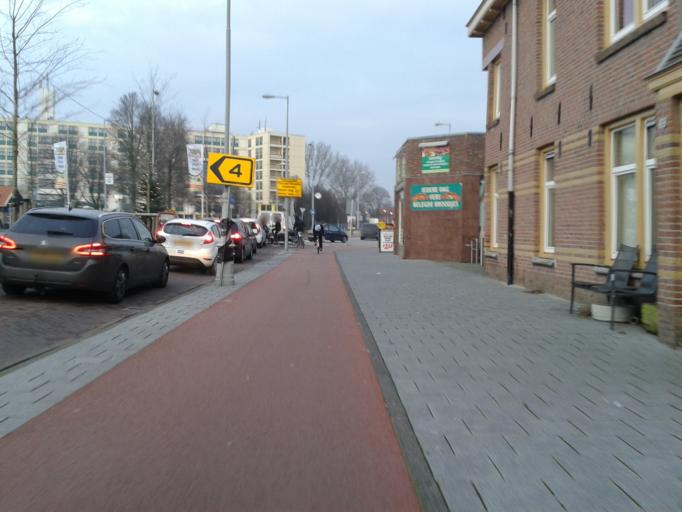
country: NL
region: North Holland
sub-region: Gemeente Amsterdam
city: Amsterdam
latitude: 52.3906
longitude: 4.9111
